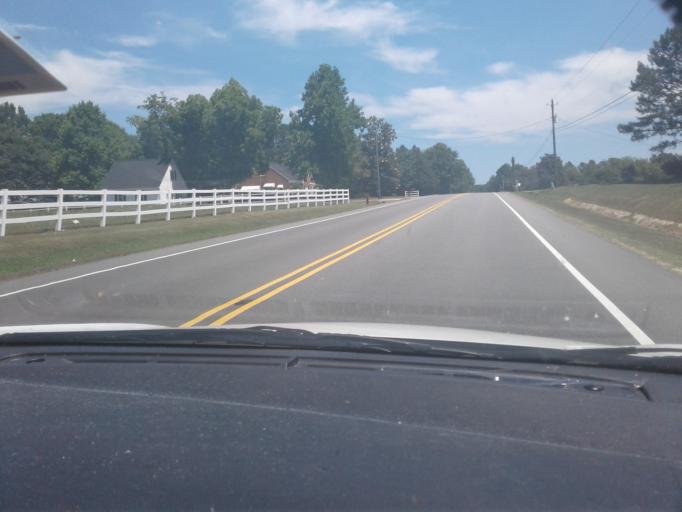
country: US
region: North Carolina
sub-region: Harnett County
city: Lillington
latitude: 35.4625
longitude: -78.8298
